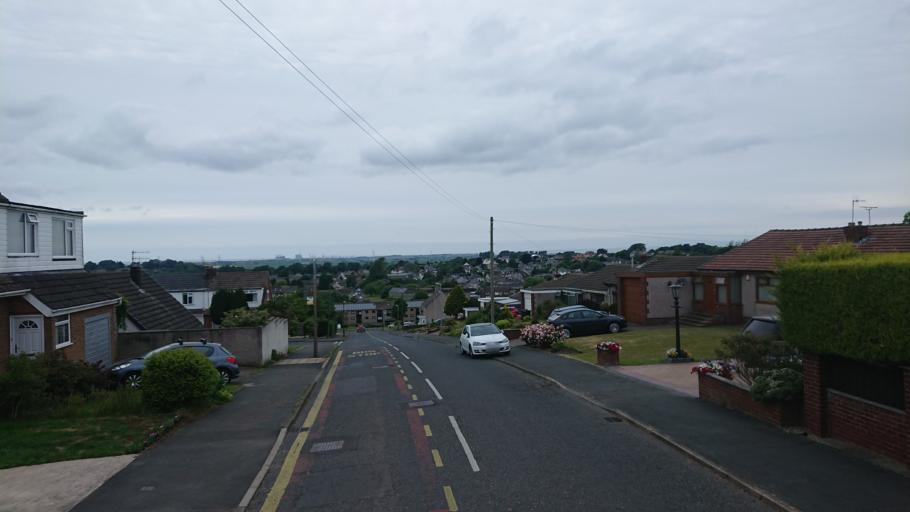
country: GB
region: England
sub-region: Lancashire
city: Lancaster
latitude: 54.0270
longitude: -2.7855
